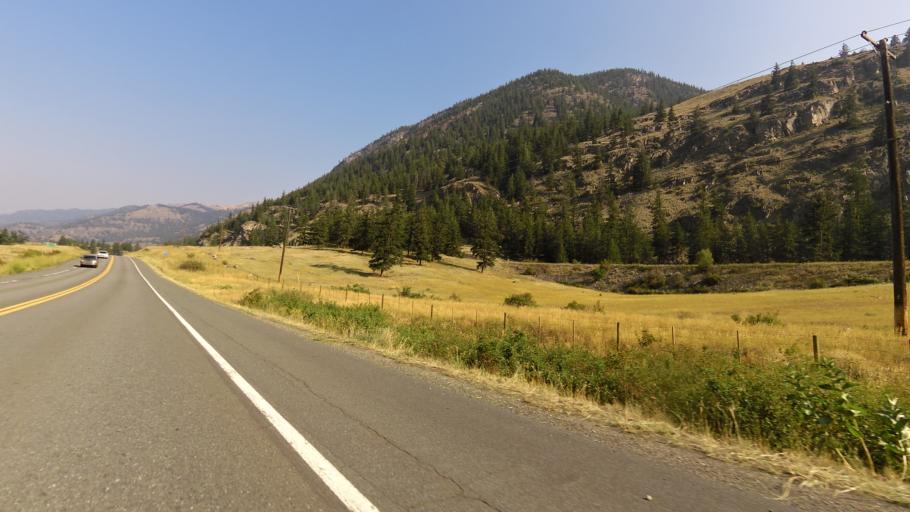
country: CA
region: British Columbia
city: Summerland
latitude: 49.3386
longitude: -120.0562
